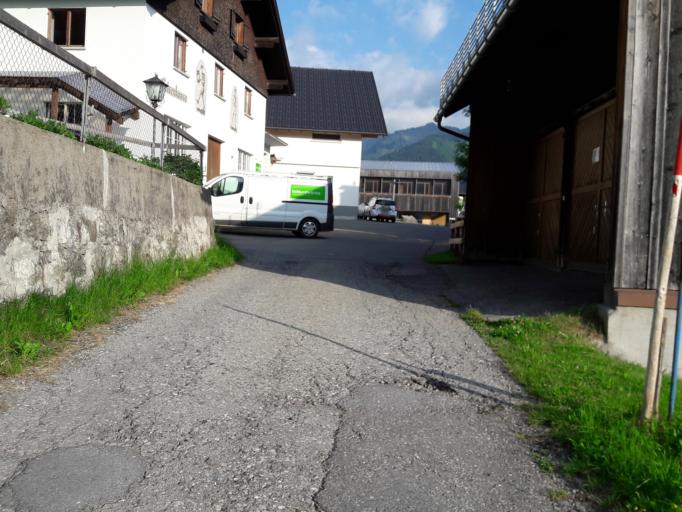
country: AT
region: Vorarlberg
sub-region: Politischer Bezirk Bludenz
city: Raggal
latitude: 47.2104
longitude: 9.8383
